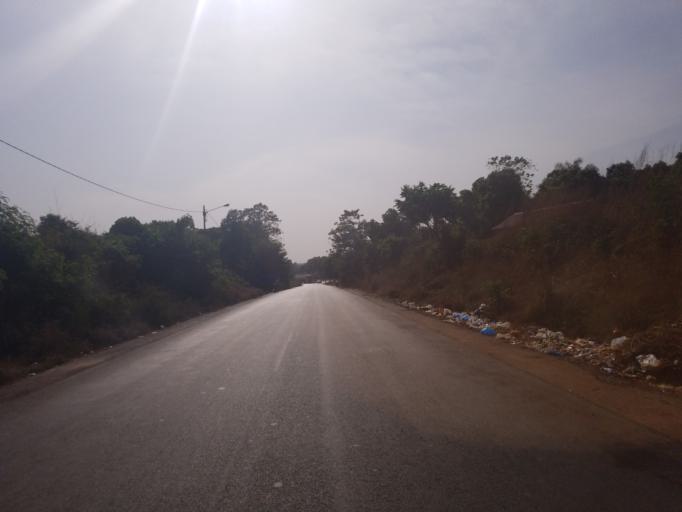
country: GN
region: Boke
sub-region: Boffa
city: Boffa
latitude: 10.1881
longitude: -14.0432
